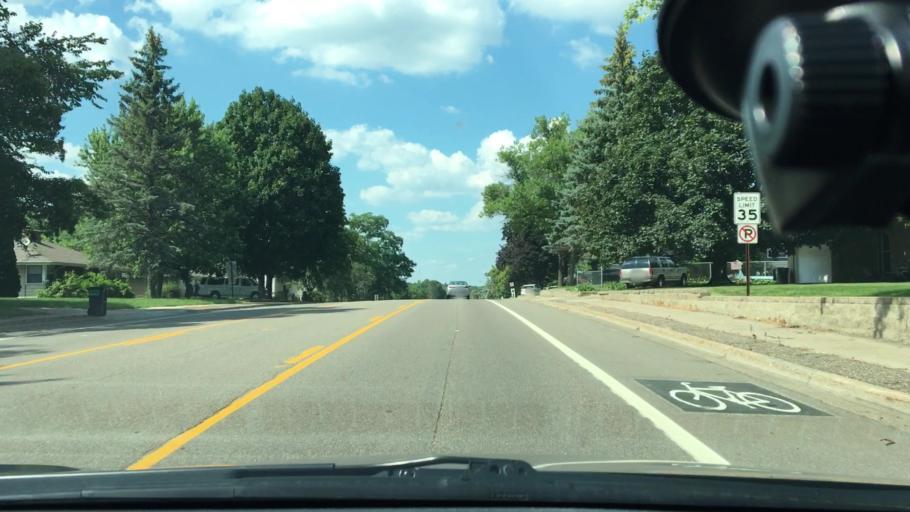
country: US
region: Minnesota
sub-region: Hennepin County
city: Golden Valley
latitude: 45.0002
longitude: -93.3803
